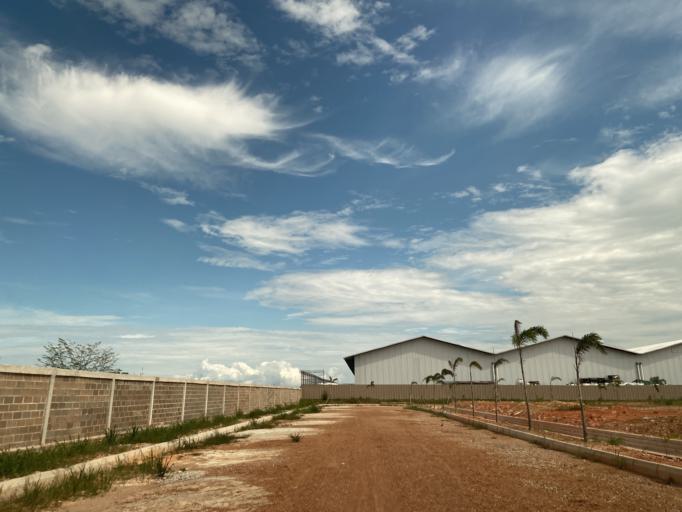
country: SG
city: Singapore
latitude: 1.0205
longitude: 103.9554
